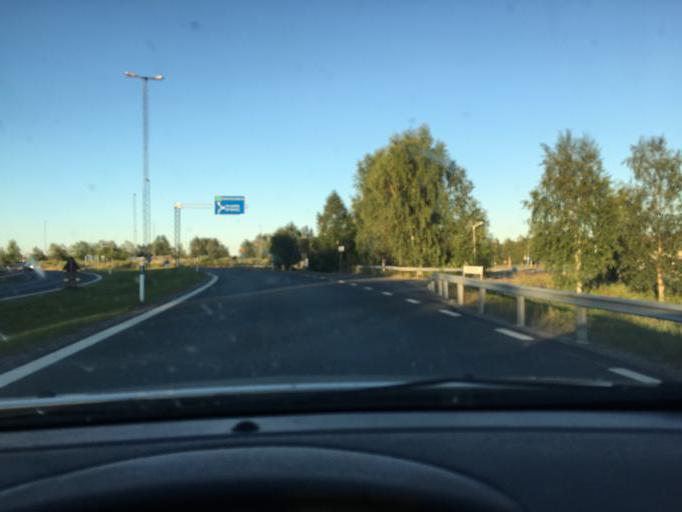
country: SE
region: Norrbotten
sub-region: Kalix Kommun
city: Rolfs
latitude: 65.8510
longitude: 23.1201
